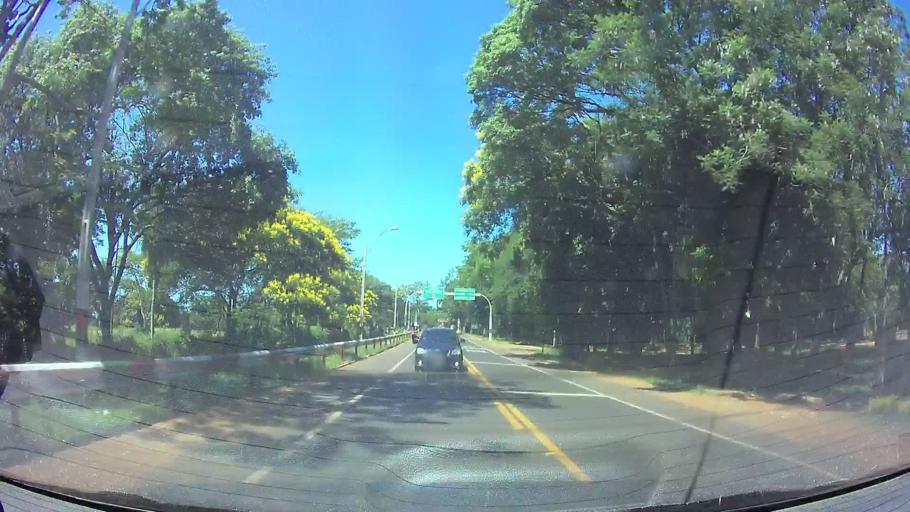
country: PY
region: Central
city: Aregua
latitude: -25.3212
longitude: -57.3900
